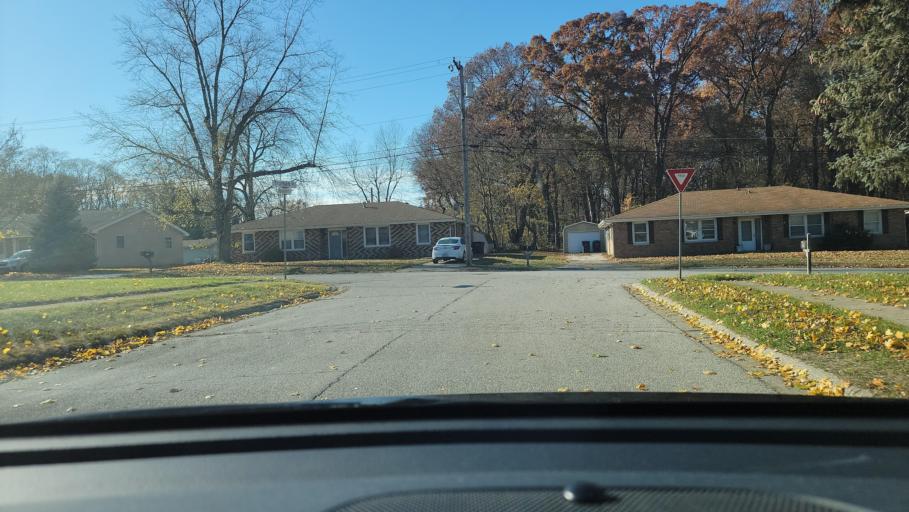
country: US
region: Indiana
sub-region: Porter County
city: Burns Harbor
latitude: 41.5978
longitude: -87.1481
